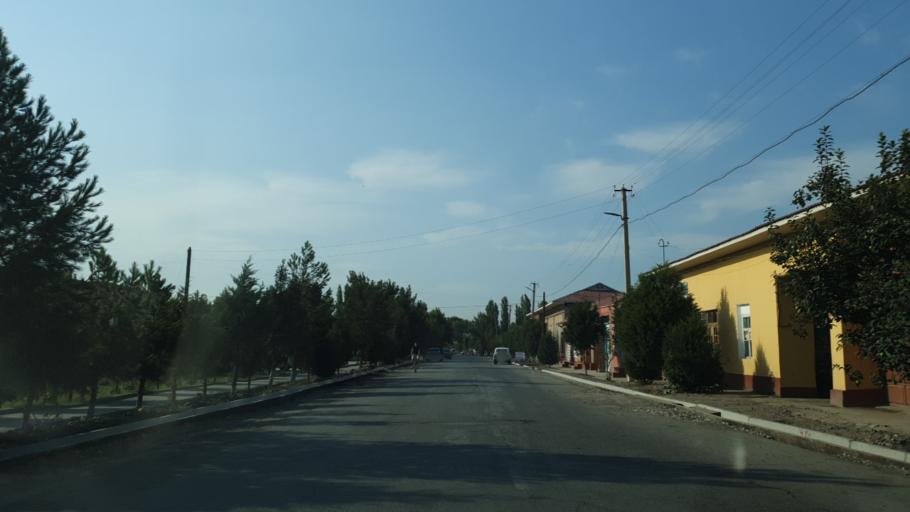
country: UZ
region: Fergana
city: Yaypan
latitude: 40.3743
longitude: 70.8125
